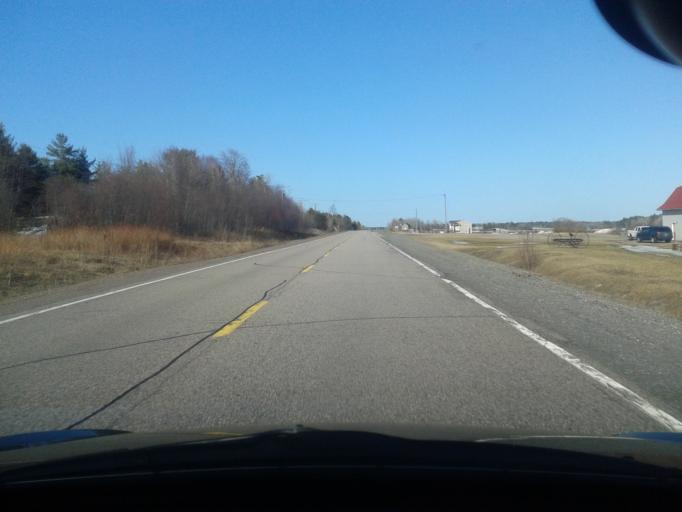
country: CA
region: Ontario
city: Greater Sudbury
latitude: 46.2712
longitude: -80.2923
